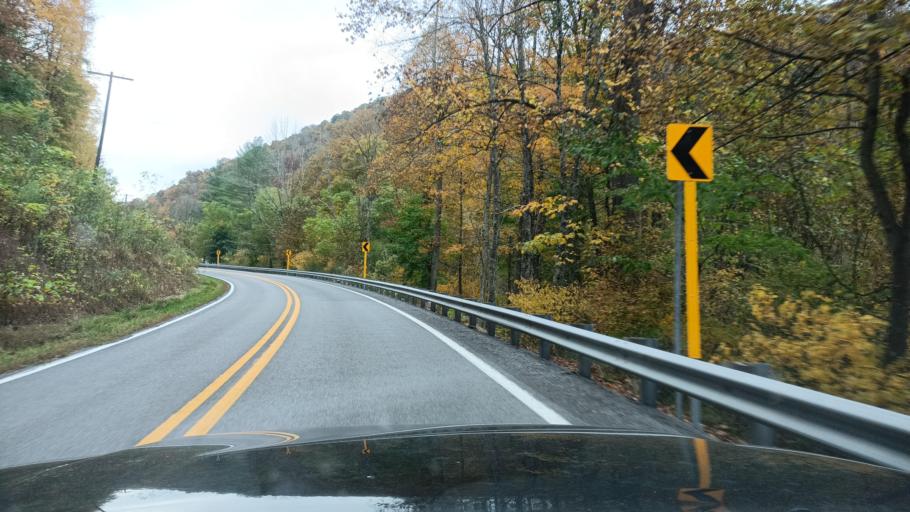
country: US
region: West Virginia
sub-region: Preston County
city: Kingwood
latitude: 39.3263
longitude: -79.6687
